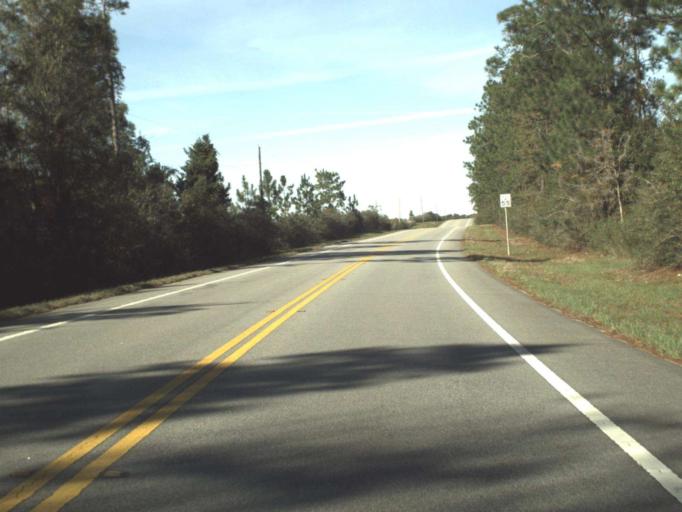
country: US
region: Florida
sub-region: Escambia County
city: Molino
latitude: 30.7998
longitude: -87.4233
